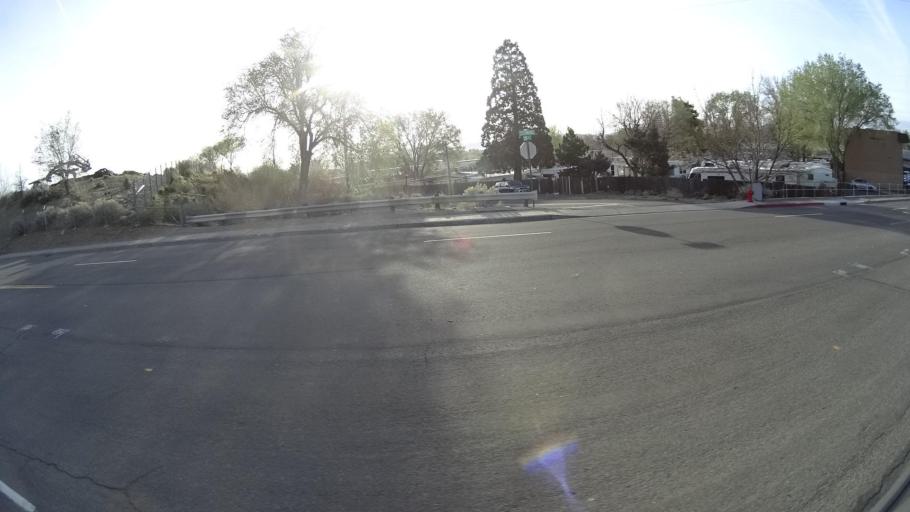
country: US
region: Nevada
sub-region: Washoe County
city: Reno
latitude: 39.5251
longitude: -119.8386
